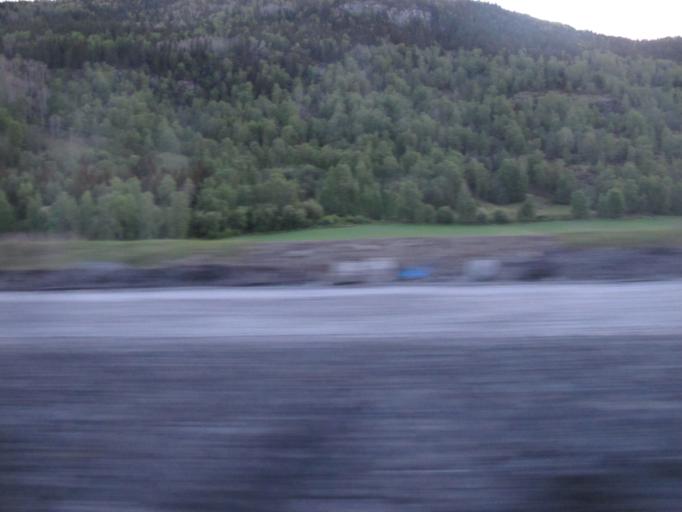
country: NO
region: Oppland
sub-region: Sor-Fron
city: Hundorp
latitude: 61.5480
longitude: 10.0198
